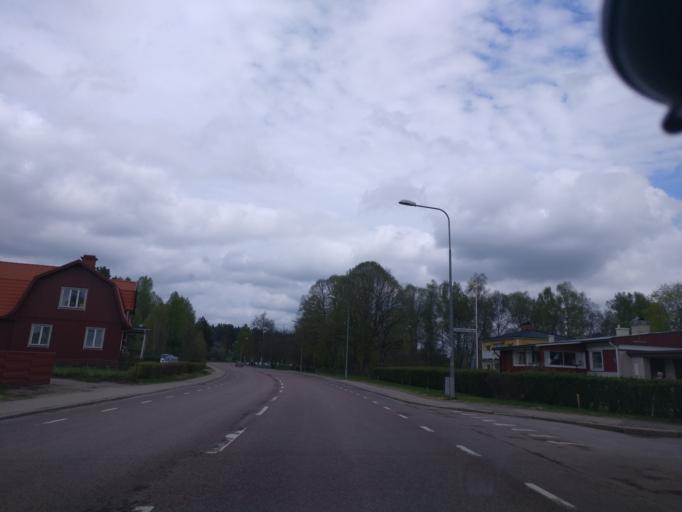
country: SE
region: Vaermland
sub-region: Hagfors Kommun
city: Ekshaerad
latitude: 60.1791
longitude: 13.4963
